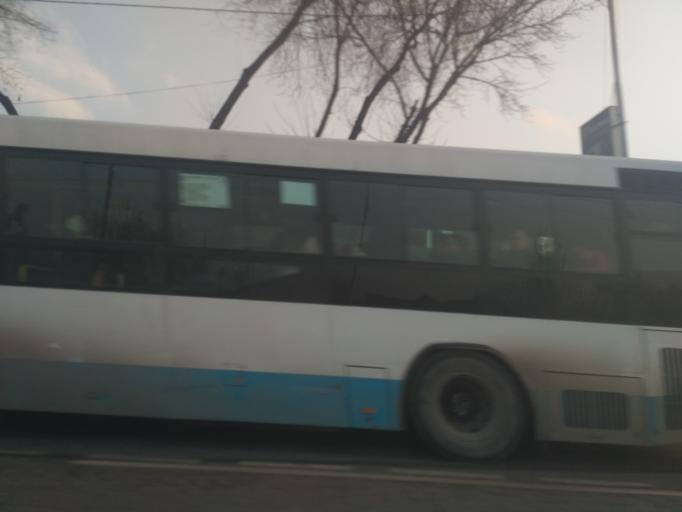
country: KZ
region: Almaty Qalasy
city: Almaty
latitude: 43.2483
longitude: 76.8437
